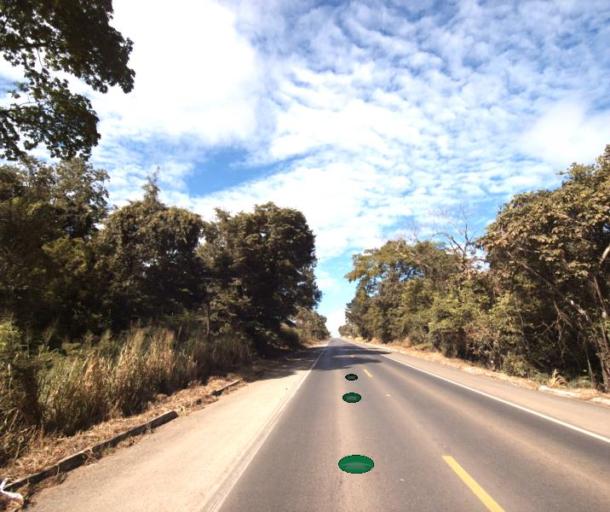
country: BR
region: Goias
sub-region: Uruacu
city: Uruacu
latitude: -14.6909
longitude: -49.2125
